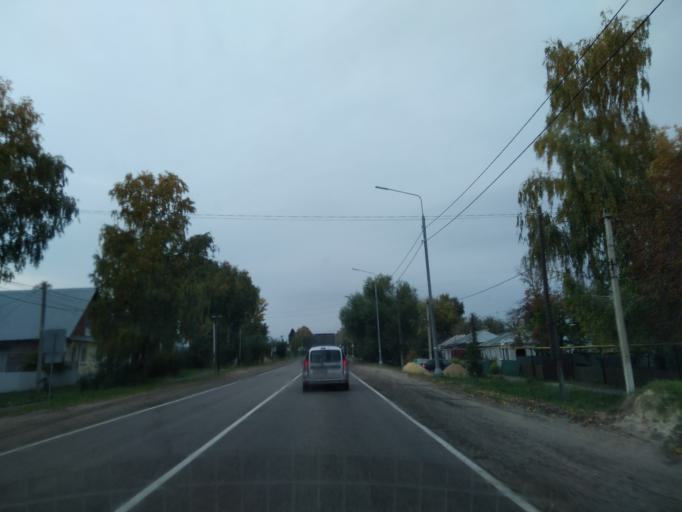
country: RU
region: Lipetsk
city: Zadonsk
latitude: 52.4150
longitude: 38.8641
